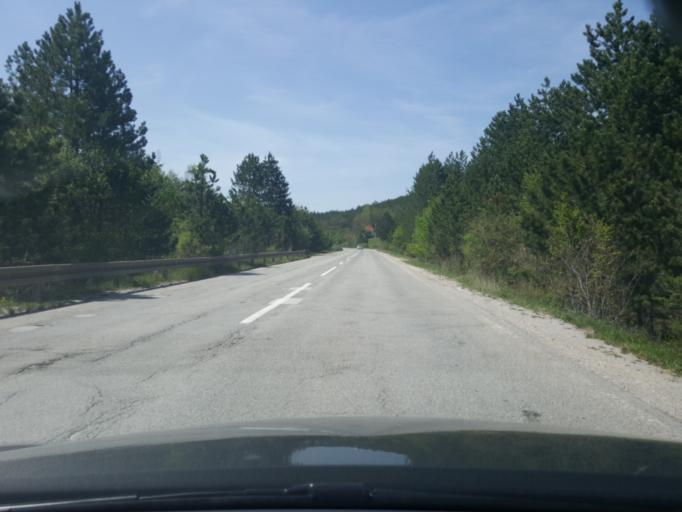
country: RS
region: Central Serbia
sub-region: Zlatiborski Okrug
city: Cajetina
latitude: 43.7876
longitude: 19.6638
